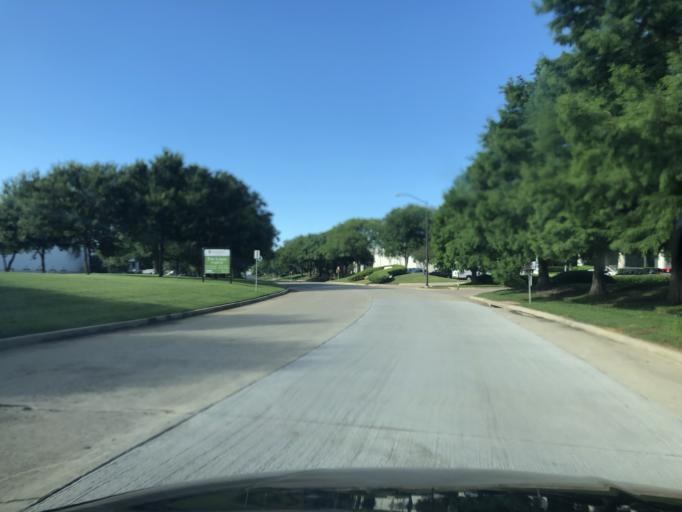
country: US
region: Texas
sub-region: Tarrant County
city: Euless
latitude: 32.8313
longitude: -97.0440
